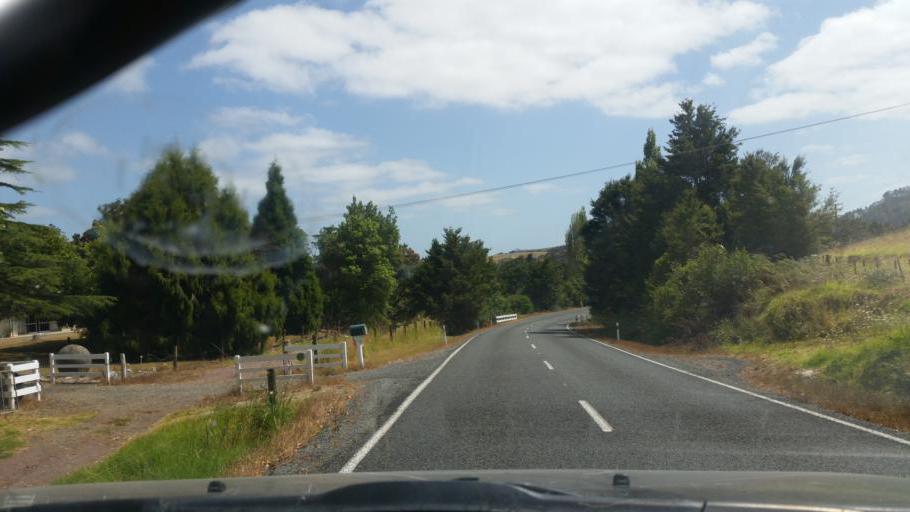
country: NZ
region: Northland
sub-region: Whangarei
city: Ruakaka
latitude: -35.9444
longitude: 174.2916
